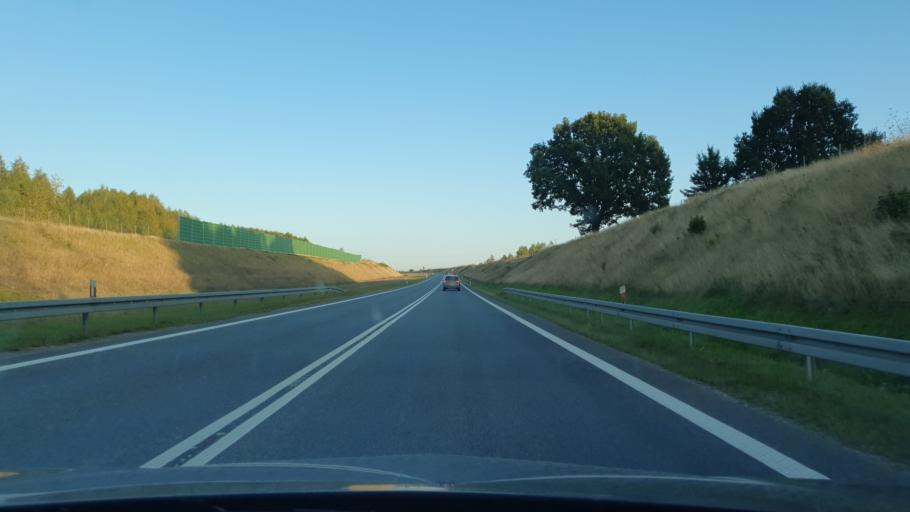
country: PL
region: Pomeranian Voivodeship
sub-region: Powiat slupski
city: Kobylnica
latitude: 54.4300
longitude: 16.9763
